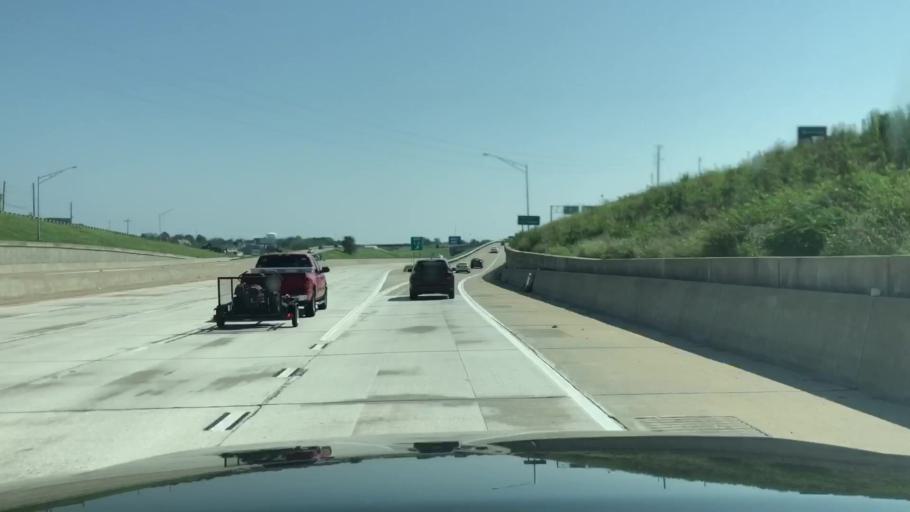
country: US
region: Missouri
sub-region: Saint Charles County
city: Saint Charles
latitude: 38.7529
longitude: -90.5533
